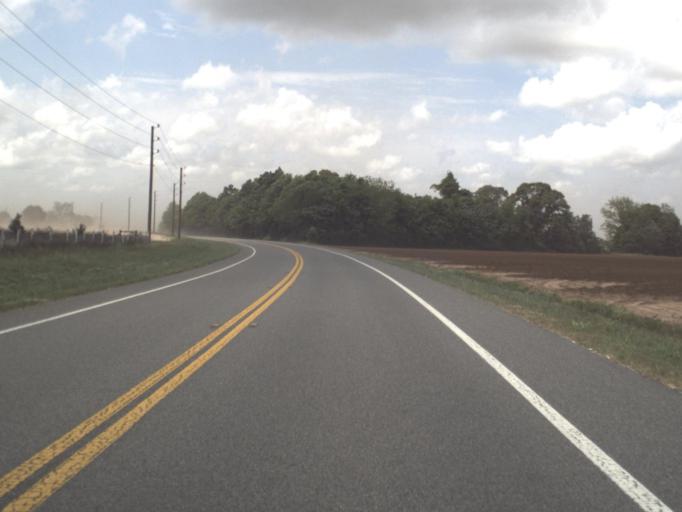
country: US
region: Florida
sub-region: Santa Rosa County
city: Point Baker
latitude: 30.8039
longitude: -87.0945
